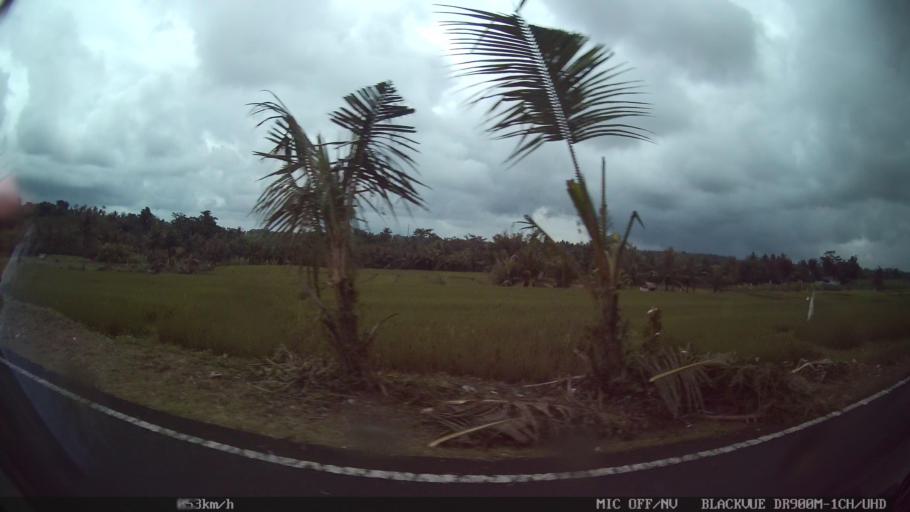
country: ID
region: Bali
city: Banjar Cemenggon
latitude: -8.5384
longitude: 115.1870
